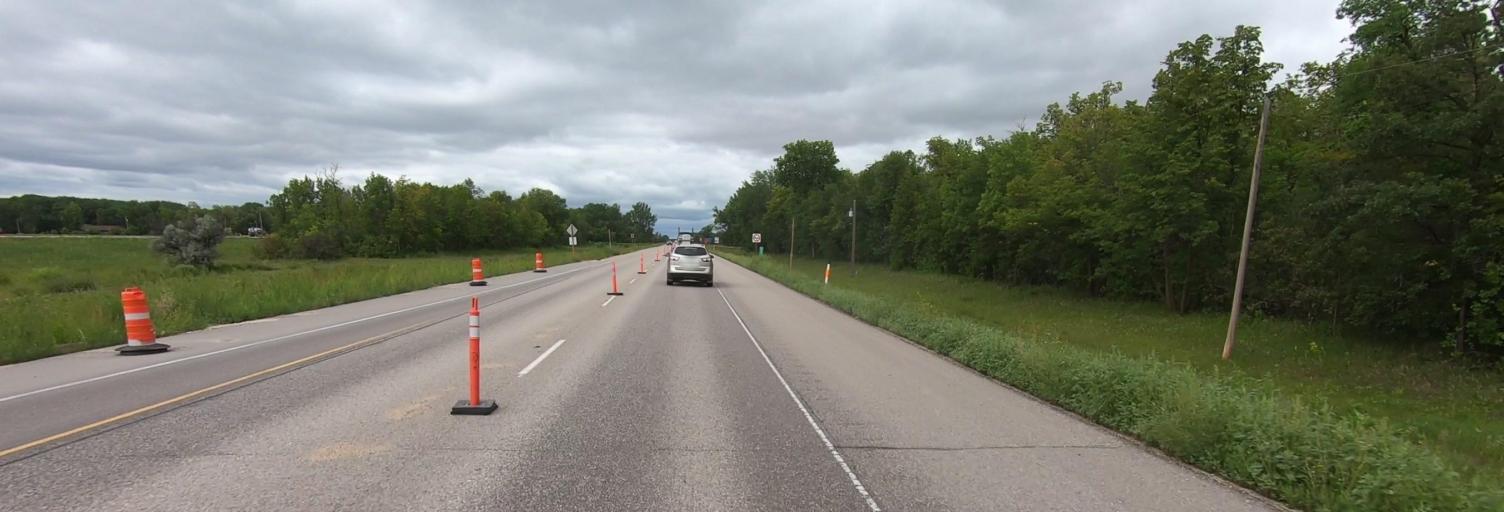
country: CA
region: Manitoba
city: Portage la Prairie
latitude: 49.9682
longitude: -98.0867
